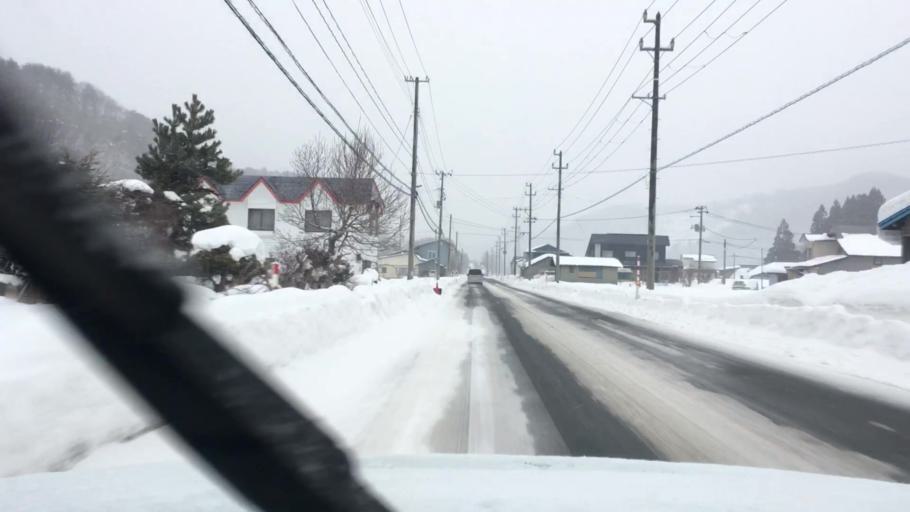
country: JP
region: Akita
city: Hanawa
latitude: 40.0564
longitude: 141.0097
